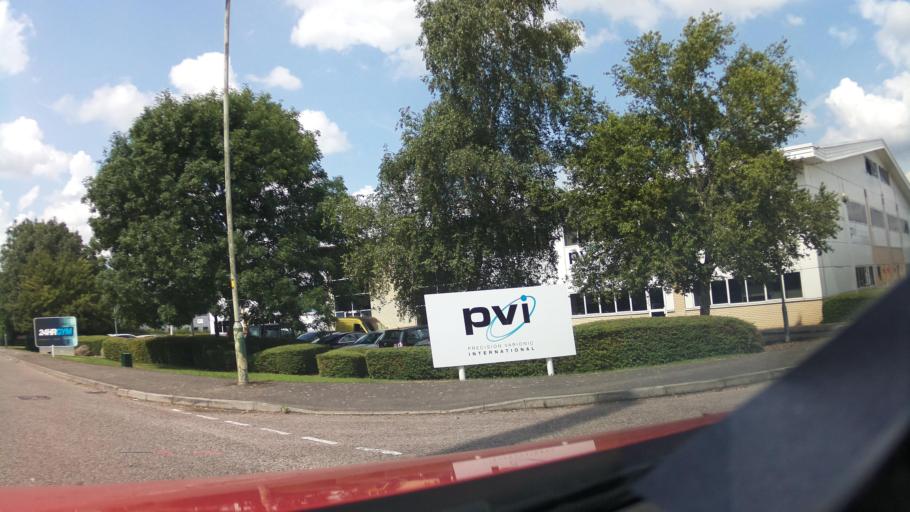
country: GB
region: England
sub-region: Wiltshire
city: Lydiard Tregoze
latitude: 51.5726
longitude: -1.8316
